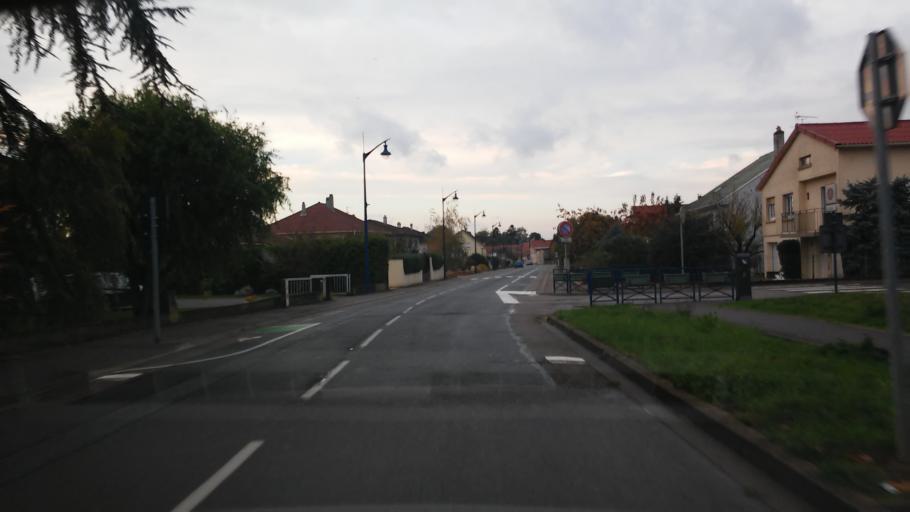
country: FR
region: Lorraine
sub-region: Departement de la Moselle
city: Ennery
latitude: 49.2226
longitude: 6.2205
